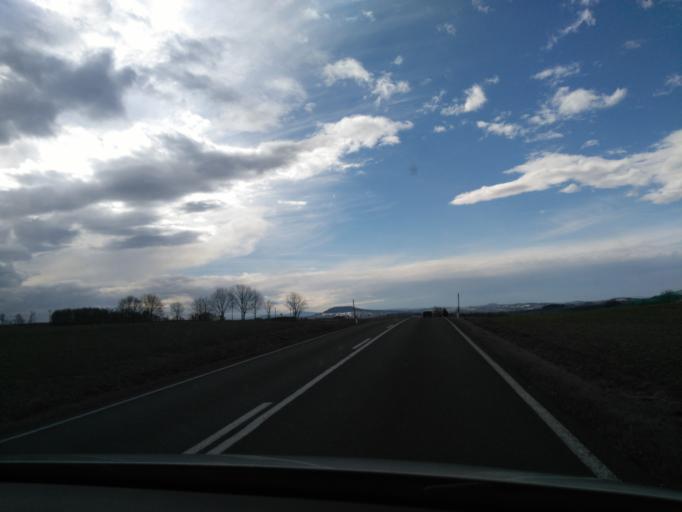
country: DE
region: Saxony
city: Wolkenstein
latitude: 50.6678
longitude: 13.1036
